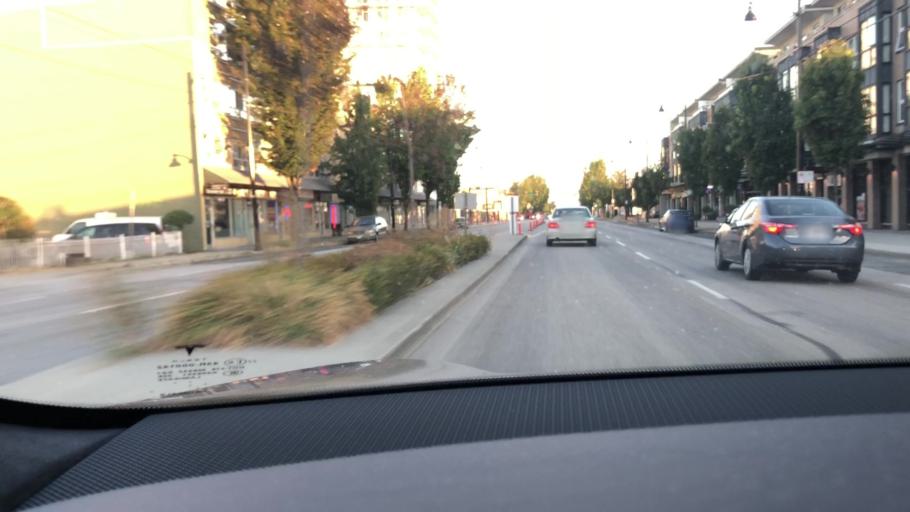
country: CA
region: British Columbia
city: Vancouver
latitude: 49.2425
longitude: -123.0593
